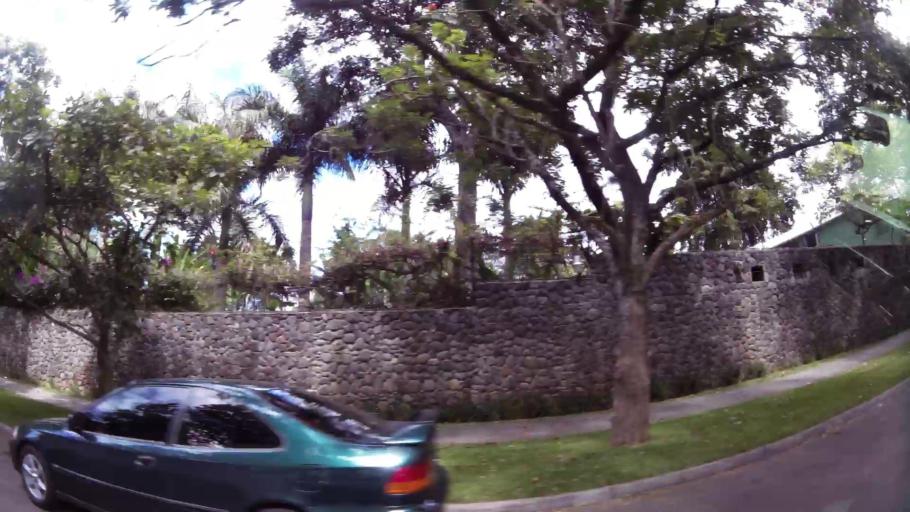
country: GT
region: Guatemala
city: Santa Catarina Pinula
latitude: 14.5877
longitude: -90.5095
